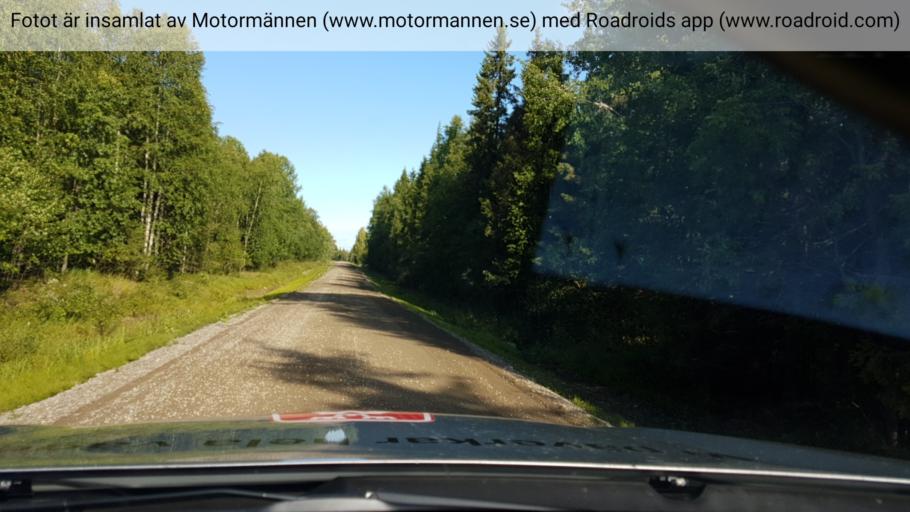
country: SE
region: Norrbotten
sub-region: Kalix Kommun
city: Kalix
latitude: 66.1979
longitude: 23.1953
